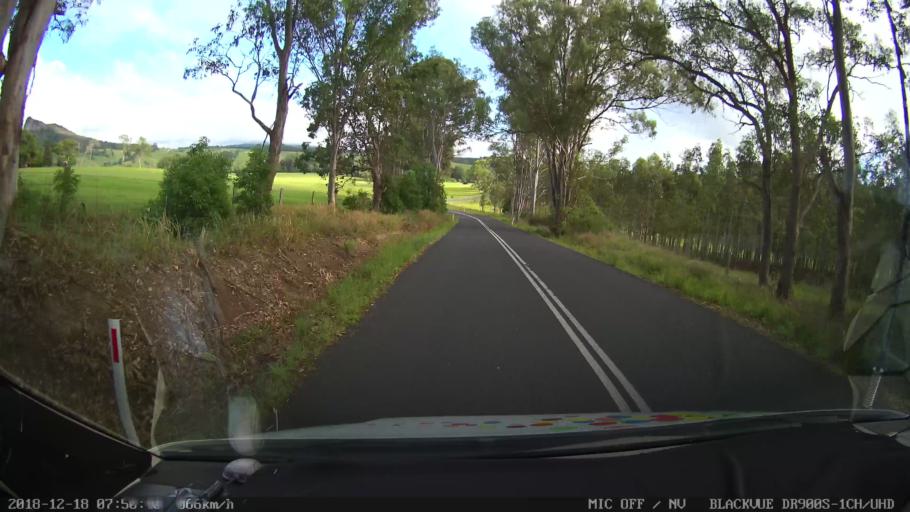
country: AU
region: New South Wales
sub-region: Kyogle
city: Kyogle
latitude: -28.4436
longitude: 152.5745
